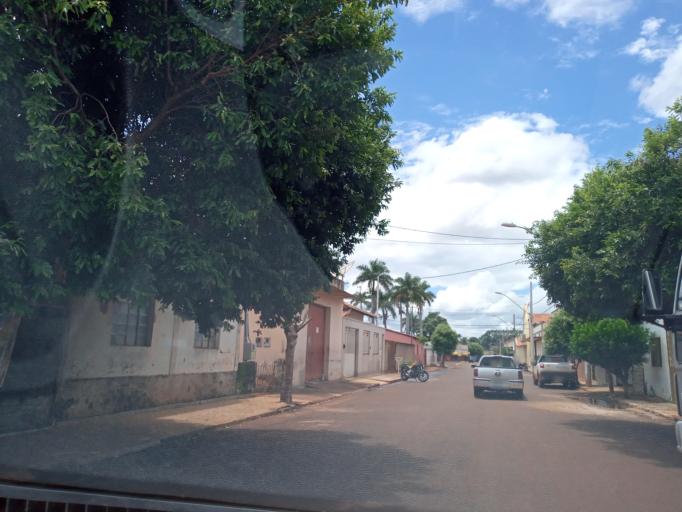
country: BR
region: Minas Gerais
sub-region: Centralina
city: Centralina
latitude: -18.5847
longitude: -49.1997
